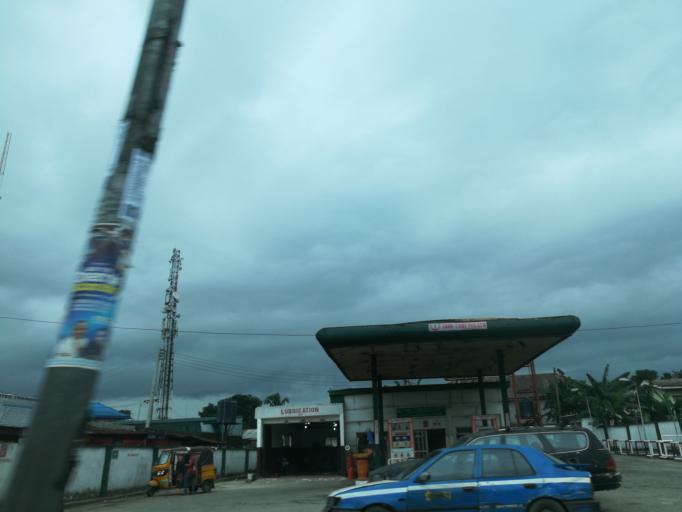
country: NG
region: Rivers
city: Port Harcourt
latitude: 4.8437
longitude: 7.0408
